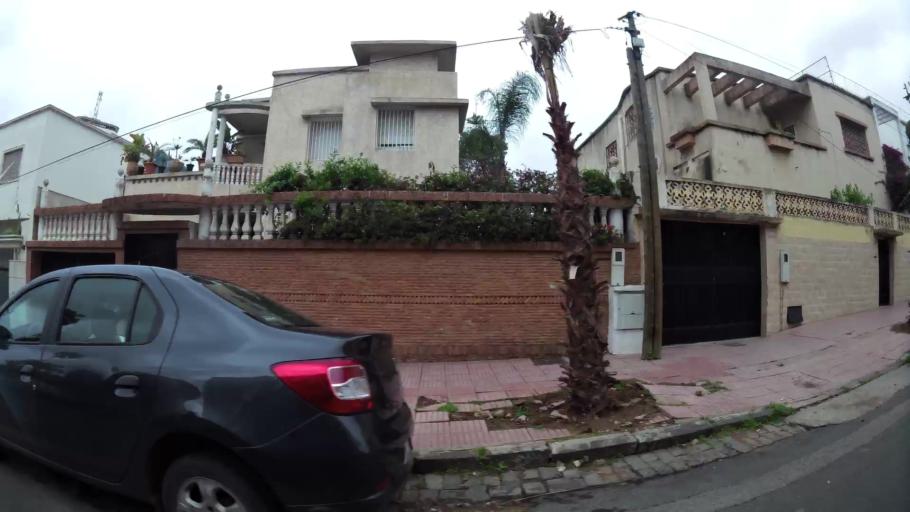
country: MA
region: Grand Casablanca
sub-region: Casablanca
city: Casablanca
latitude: 33.5826
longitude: -7.6101
